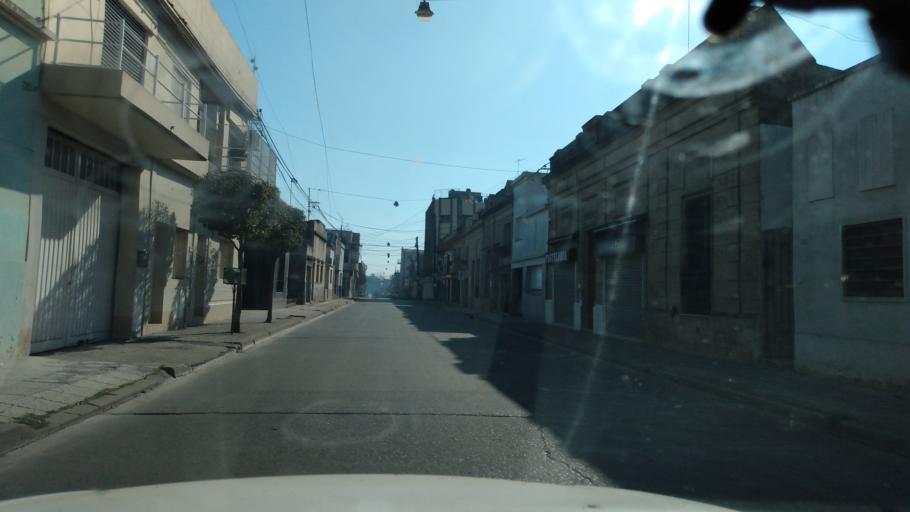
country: AR
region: Buenos Aires
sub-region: Partido de Lujan
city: Lujan
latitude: -34.5682
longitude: -59.1154
